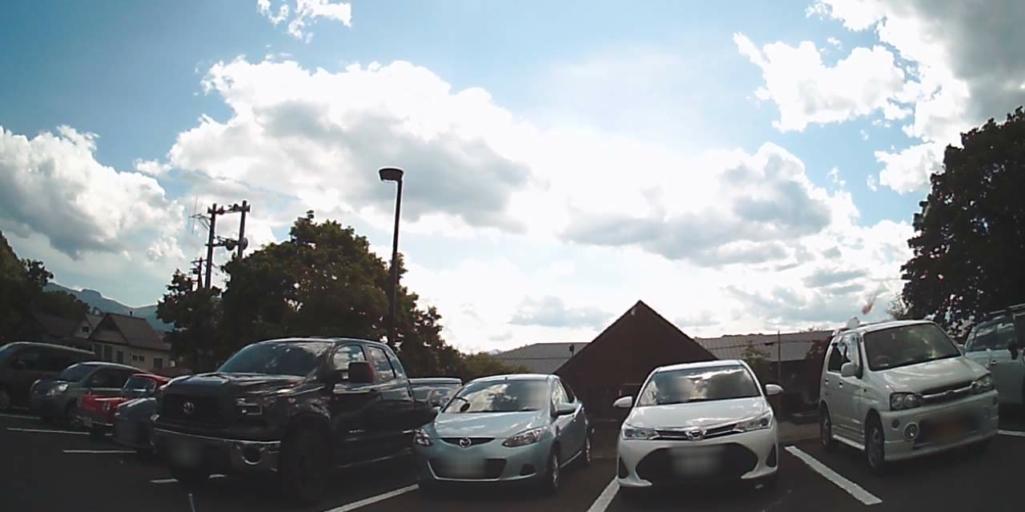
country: JP
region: Hokkaido
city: Shiraoi
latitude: 42.7724
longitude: 141.4061
